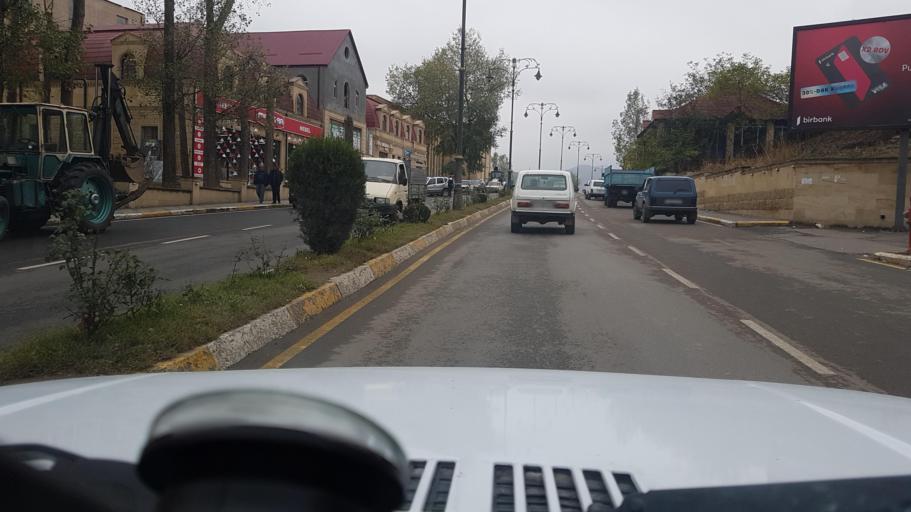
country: AZ
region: Gadabay Rayon
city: Kyadabek
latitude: 40.5772
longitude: 45.8087
